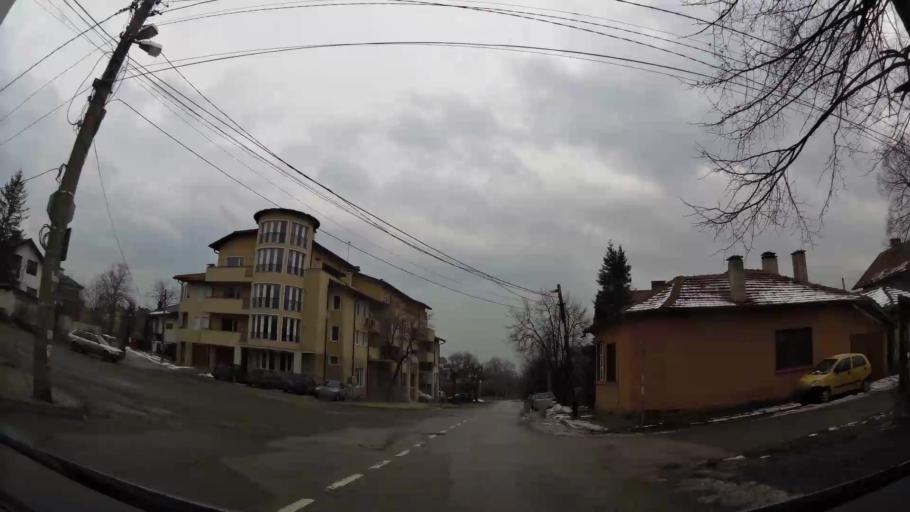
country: BG
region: Sofiya
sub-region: Obshtina Bozhurishte
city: Bozhurishte
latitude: 42.6755
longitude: 23.2344
